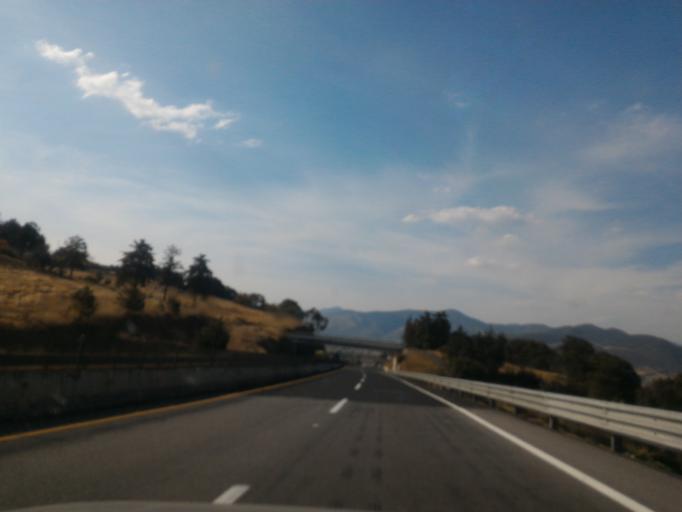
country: MX
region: Mexico
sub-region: Atlacomulco
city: La Mesa de Chosto
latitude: 19.8414
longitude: -99.8730
